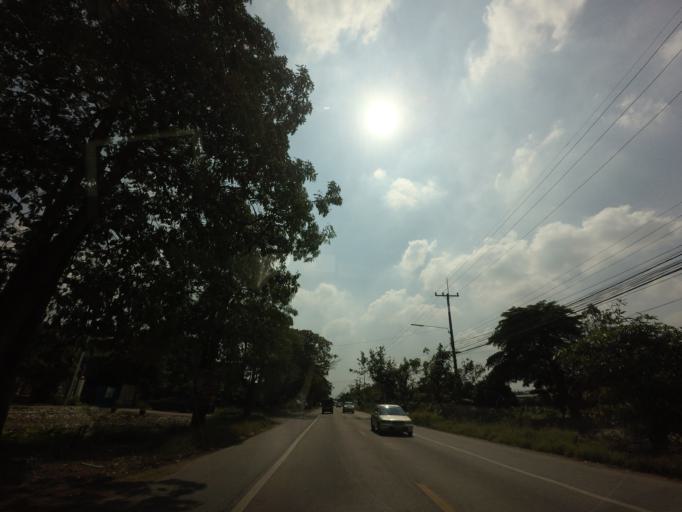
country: TH
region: Nakhon Pathom
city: Sam Phran
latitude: 13.7629
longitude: 100.2311
